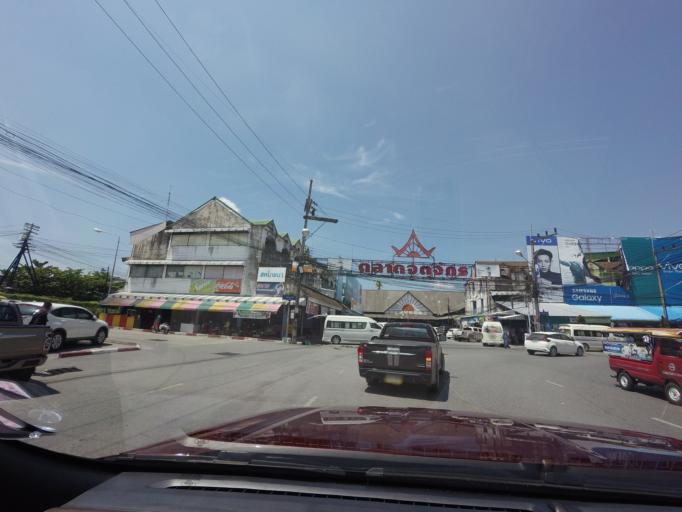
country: TH
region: Yala
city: Yala
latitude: 6.5595
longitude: 101.2932
